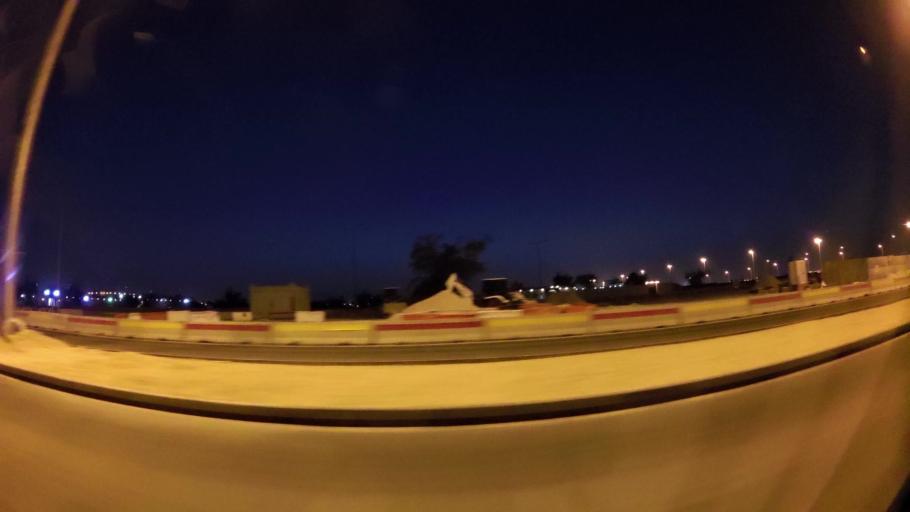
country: QA
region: Baladiyat ar Rayyan
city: Ar Rayyan
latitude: 25.2990
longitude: 51.4301
